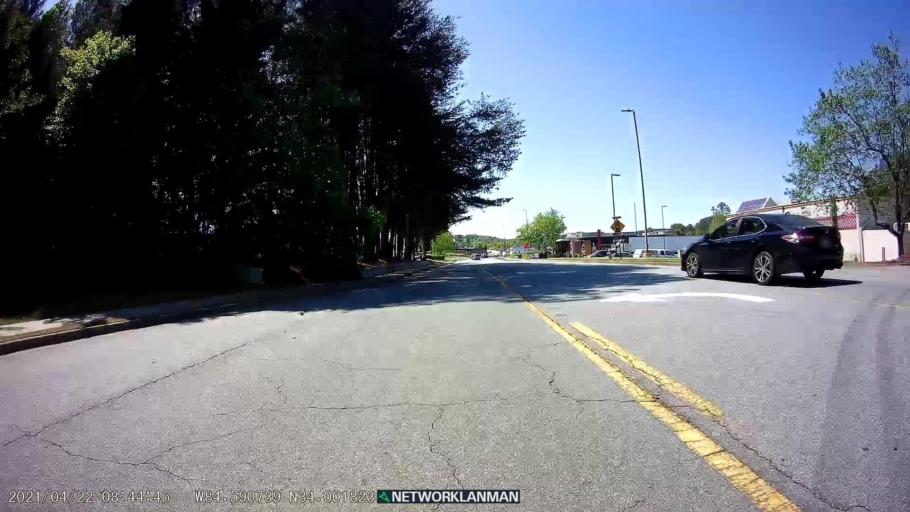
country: US
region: Georgia
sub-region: Cobb County
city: Kennesaw
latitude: 33.9992
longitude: -84.5939
